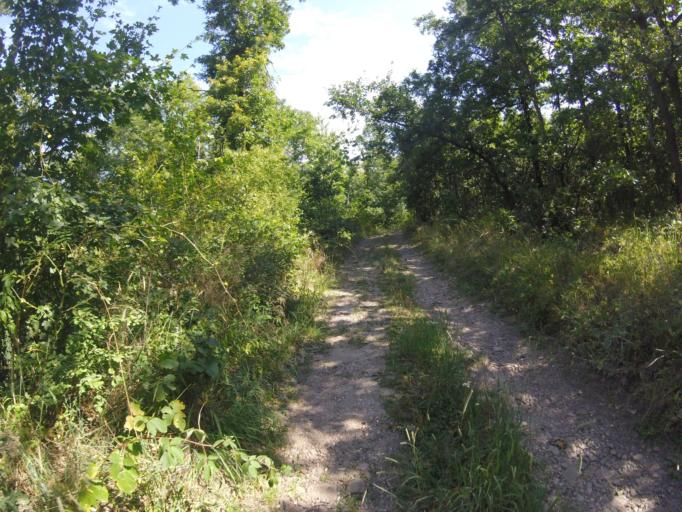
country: HU
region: Pest
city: Csobanka
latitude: 47.6819
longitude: 18.9791
